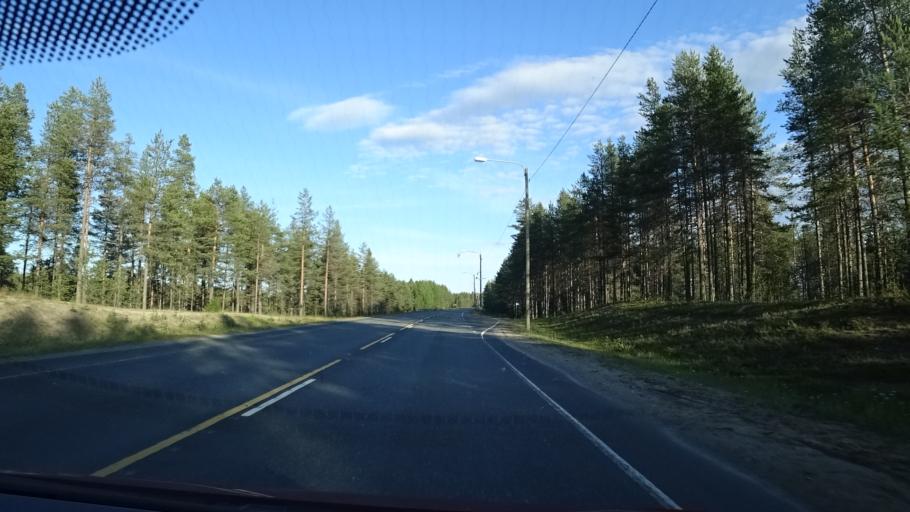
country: FI
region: Northern Ostrobothnia
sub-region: Koillismaa
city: Kuusamo
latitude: 66.0143
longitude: 29.1440
